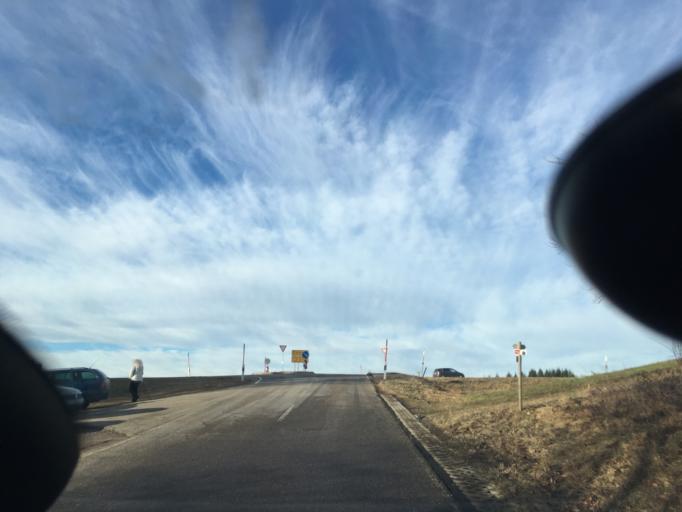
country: DE
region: Baden-Wuerttemberg
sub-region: Freiburg Region
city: Hochenschwand
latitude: 47.7240
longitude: 8.1561
